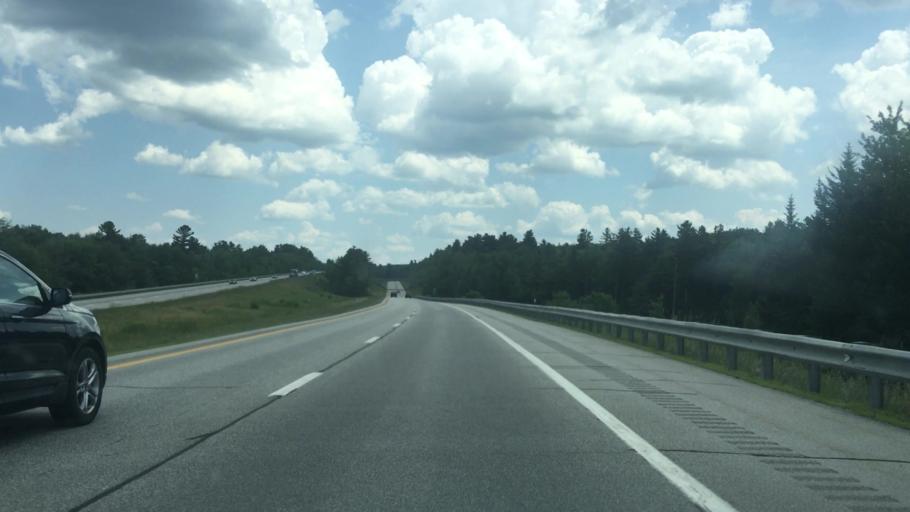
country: US
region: New Hampshire
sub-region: Merrimack County
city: New London
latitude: 43.4056
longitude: -72.0227
